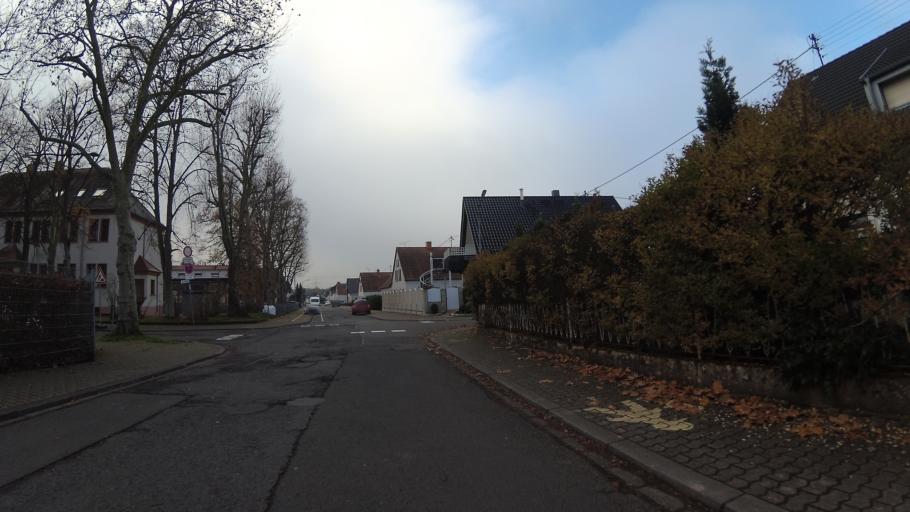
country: DE
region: Saarland
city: Schwalbach
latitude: 49.2998
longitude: 6.8021
